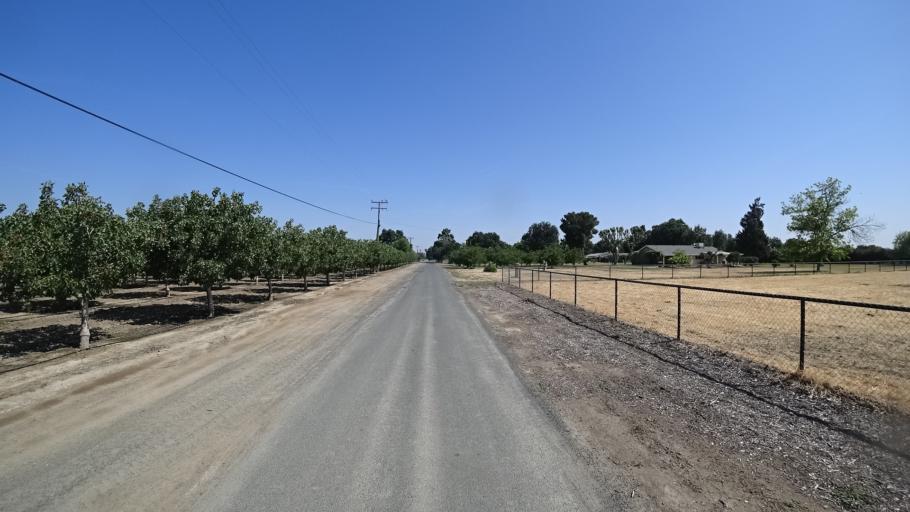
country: US
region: California
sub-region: Kings County
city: Lemoore
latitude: 36.3410
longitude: -119.8429
